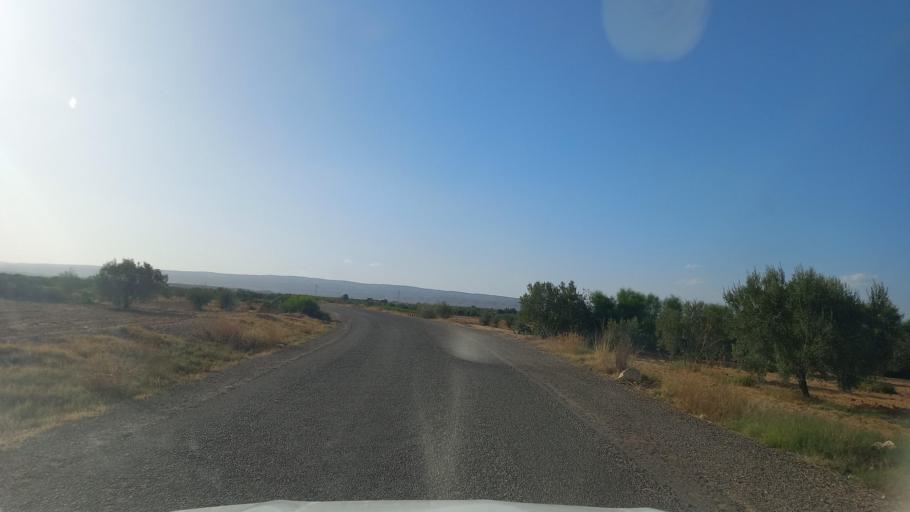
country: TN
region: Al Qasrayn
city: Kasserine
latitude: 35.2590
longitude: 9.0327
